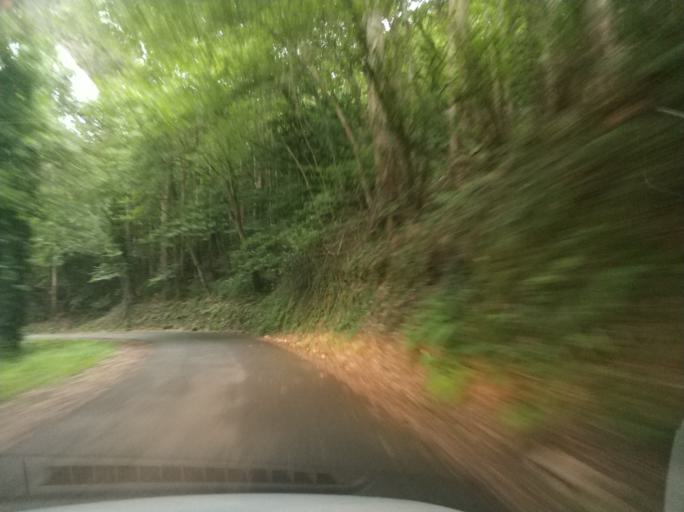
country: ES
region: Asturias
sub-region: Province of Asturias
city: Cudillero
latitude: 43.5543
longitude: -6.1908
